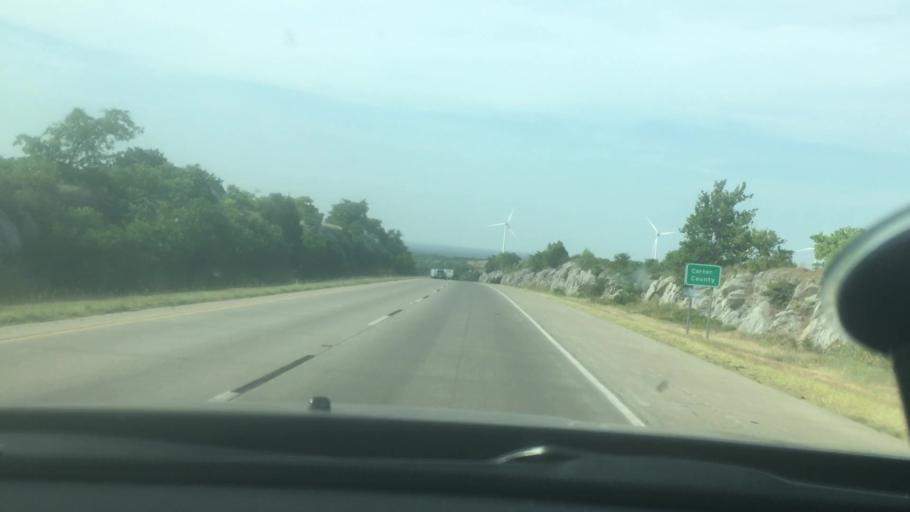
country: US
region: Oklahoma
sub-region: Murray County
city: Davis
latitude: 34.3755
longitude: -97.1451
